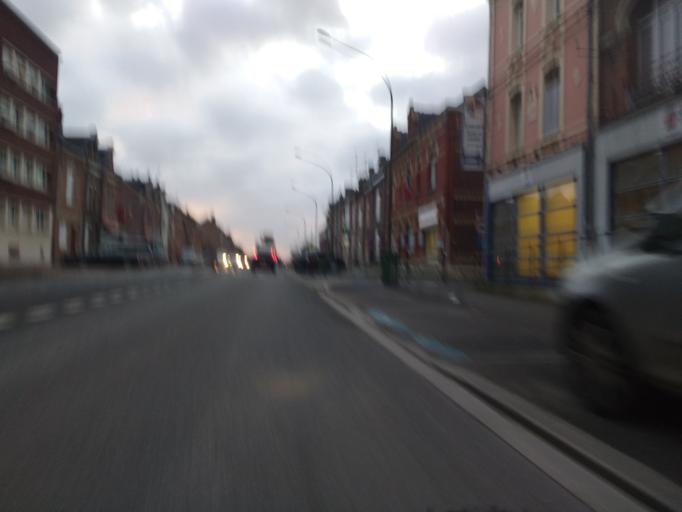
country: FR
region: Picardie
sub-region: Departement de la Somme
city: Camon
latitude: 49.8820
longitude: 2.3283
